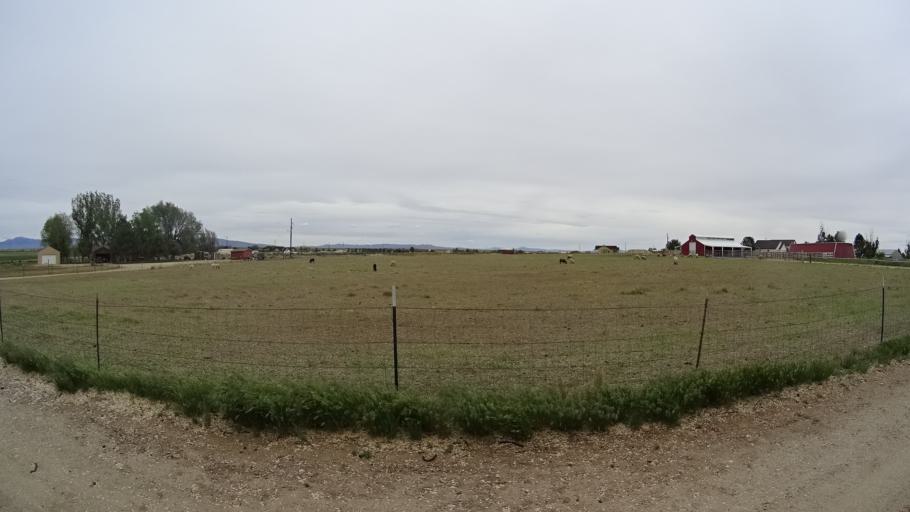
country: US
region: Idaho
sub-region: Ada County
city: Kuna
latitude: 43.4843
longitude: -116.3145
